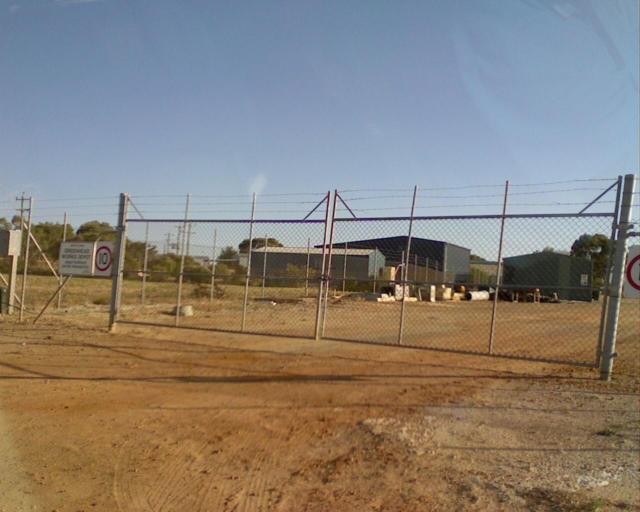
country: AU
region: Western Australia
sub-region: Dandaragan
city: Jurien Bay
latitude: -30.0538
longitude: 114.9778
